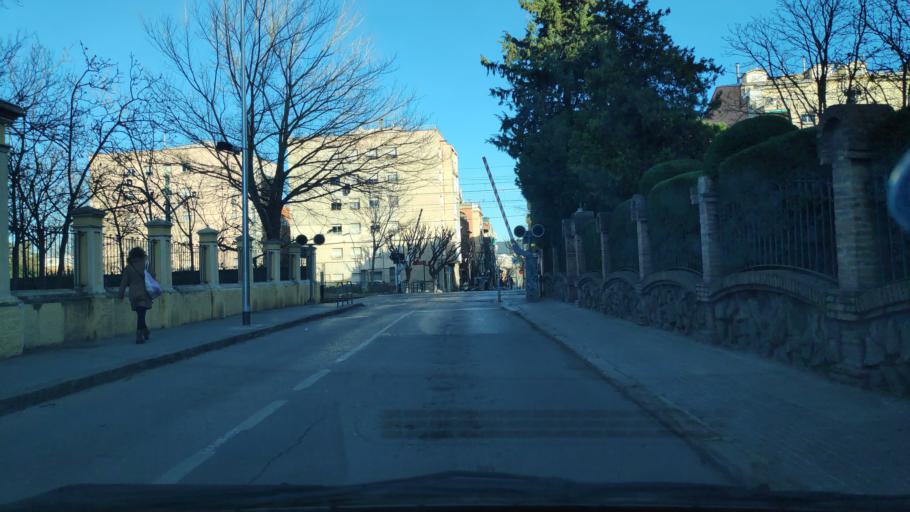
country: ES
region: Catalonia
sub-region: Provincia de Barcelona
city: Mollet del Valles
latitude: 41.5377
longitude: 2.2056
